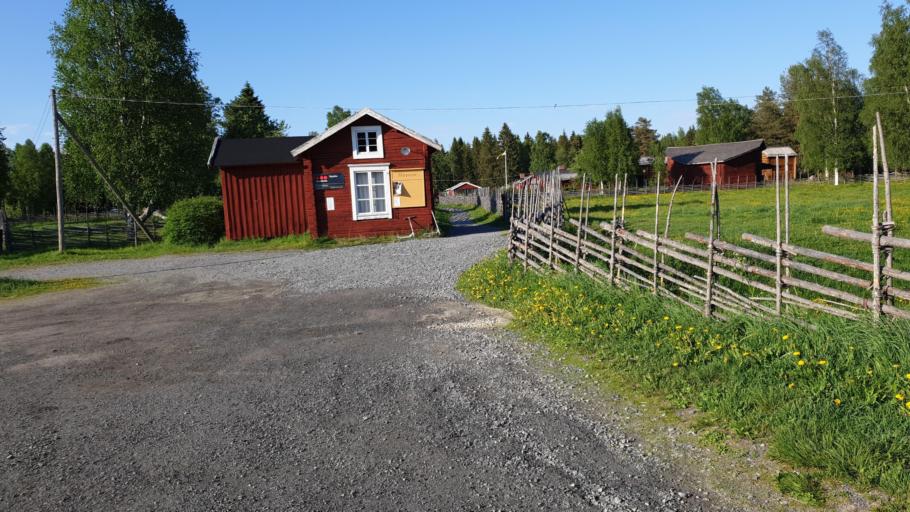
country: SE
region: Norrbotten
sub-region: Lulea Kommun
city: Gammelstad
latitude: 65.6478
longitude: 22.0340
